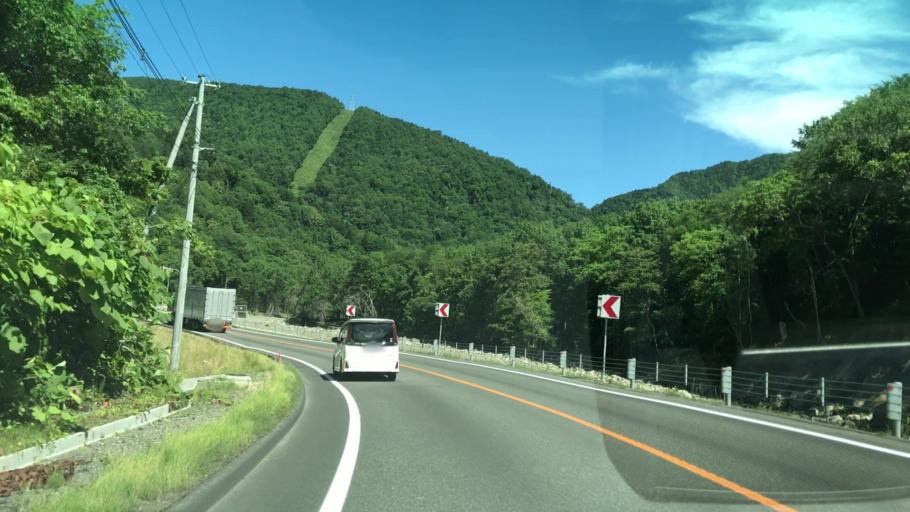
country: JP
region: Hokkaido
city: Shimo-furano
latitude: 42.9275
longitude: 142.5939
